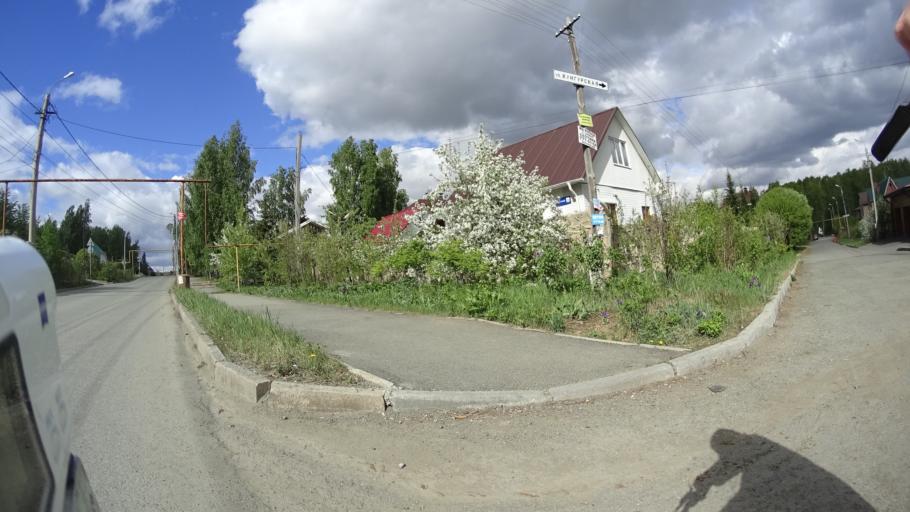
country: RU
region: Chelyabinsk
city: Sargazy
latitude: 55.1565
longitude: 61.2520
